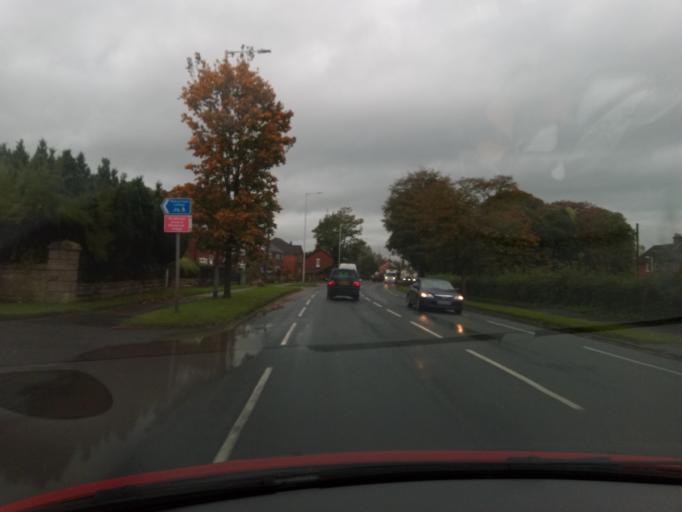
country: GB
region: England
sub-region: Lancashire
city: Catterall
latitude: 53.8546
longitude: -2.7449
